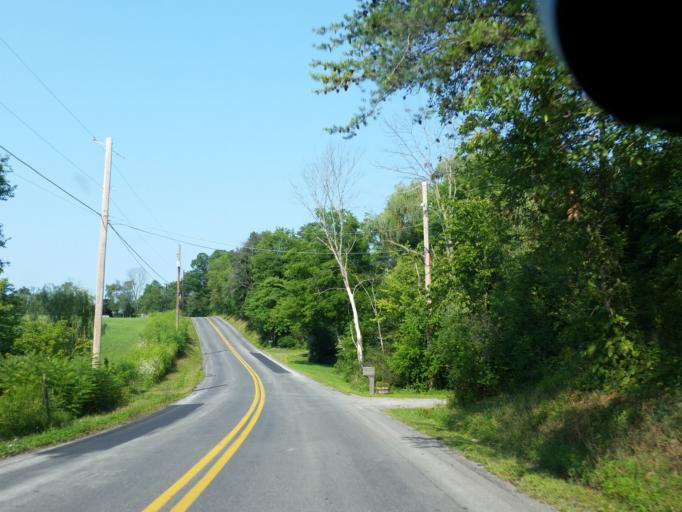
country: US
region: Pennsylvania
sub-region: Union County
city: New Columbia
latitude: 41.0510
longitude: -76.9310
